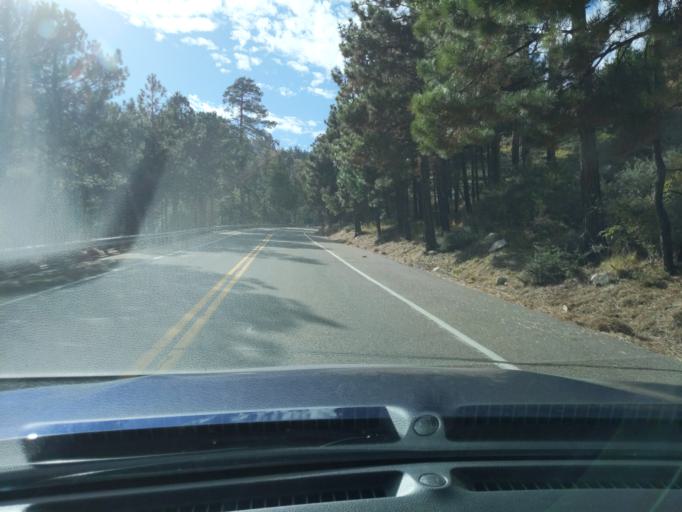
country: US
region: Arizona
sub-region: Pinal County
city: Oracle
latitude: 32.4463
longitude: -110.7602
